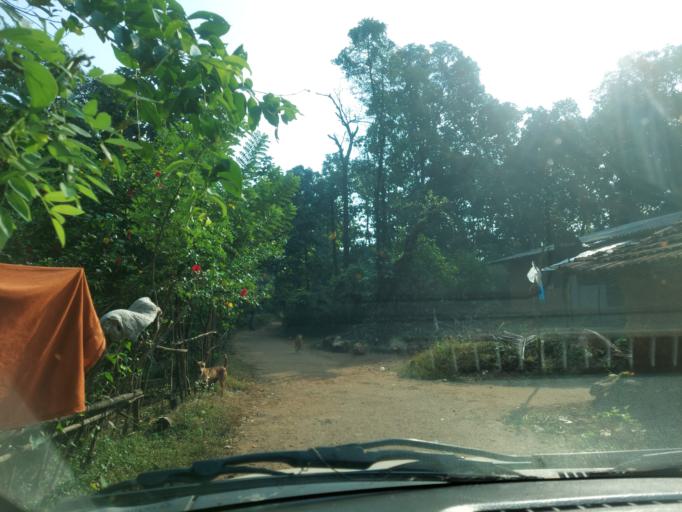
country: IN
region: Maharashtra
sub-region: Sindhudurg
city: Kudal
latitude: 16.0400
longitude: 73.6811
